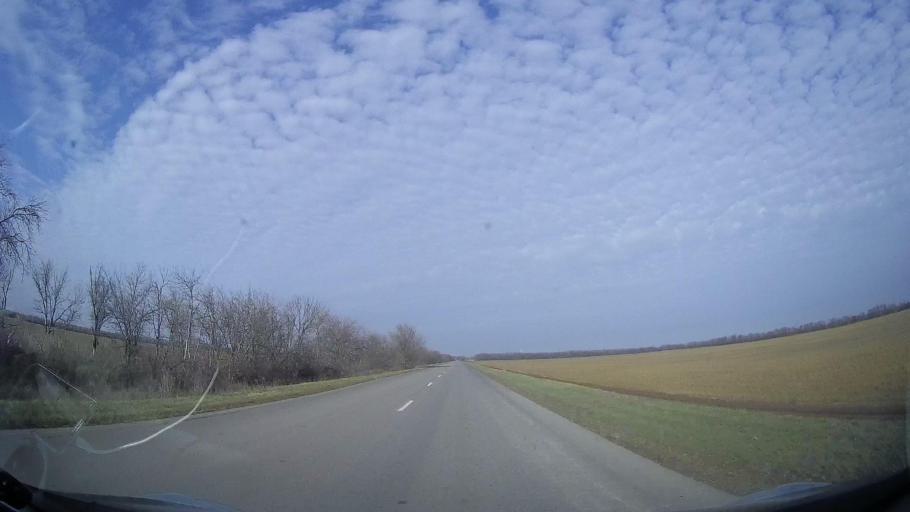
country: RU
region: Rostov
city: Gigant
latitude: 46.8237
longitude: 41.3397
